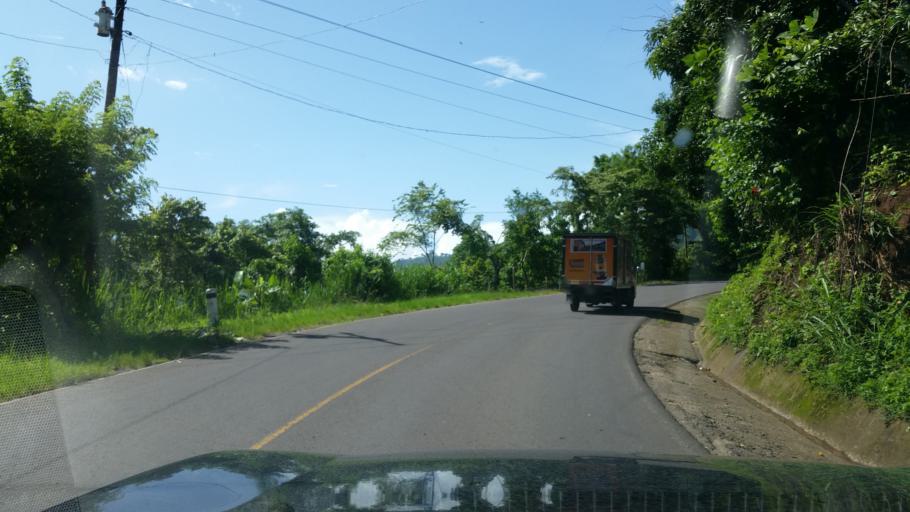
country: NI
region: Matagalpa
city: San Ramon
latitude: 13.0055
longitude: -85.8118
